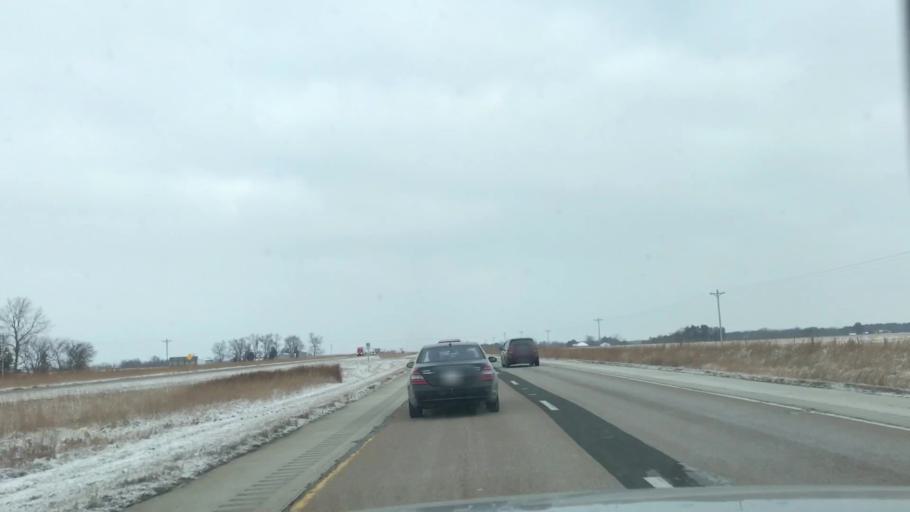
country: US
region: Illinois
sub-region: Montgomery County
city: Litchfield
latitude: 39.2364
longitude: -89.6411
